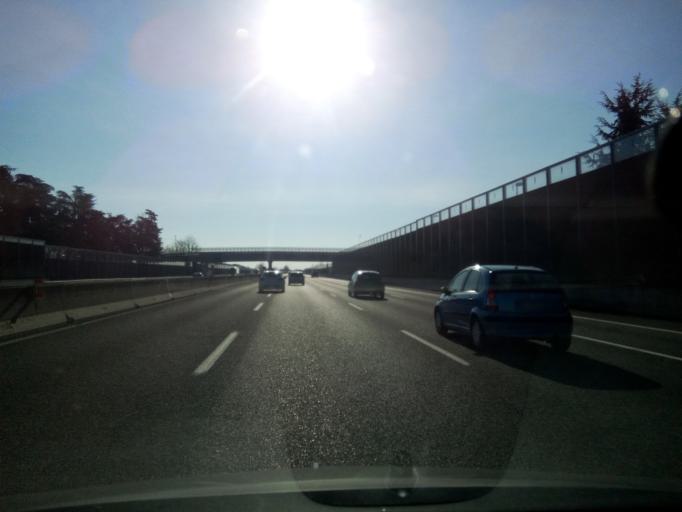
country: IT
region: Emilia-Romagna
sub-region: Provincia di Modena
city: San Cesario sul Panaro
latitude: 44.5668
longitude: 11.0345
